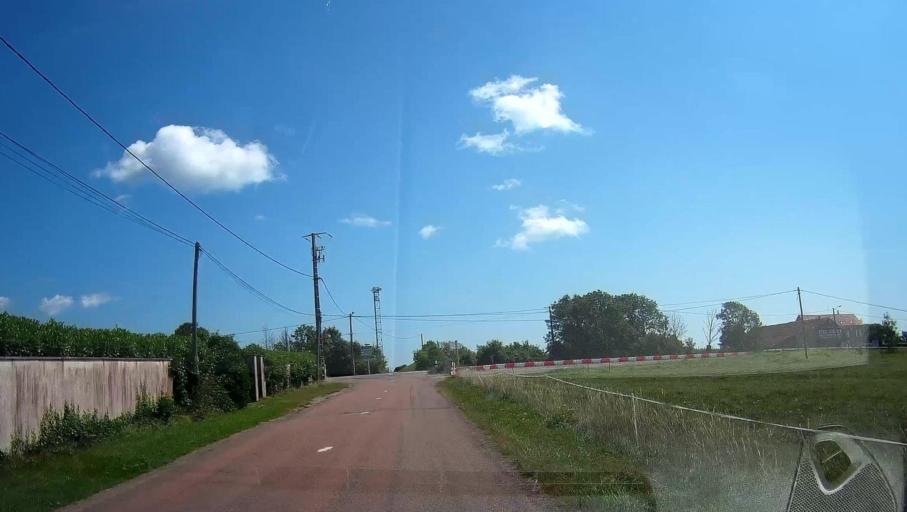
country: FR
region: Bourgogne
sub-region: Departement de la Cote-d'Or
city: Nolay
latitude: 46.9800
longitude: 4.6712
